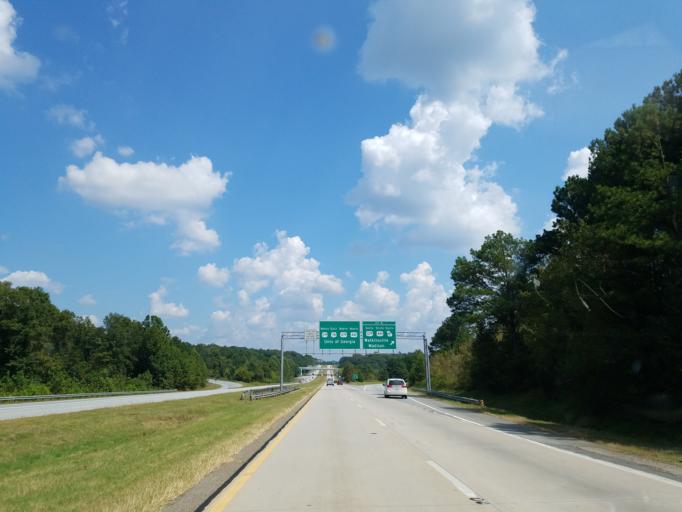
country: US
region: Georgia
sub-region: Oconee County
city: Watkinsville
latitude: 33.9160
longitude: -83.4124
